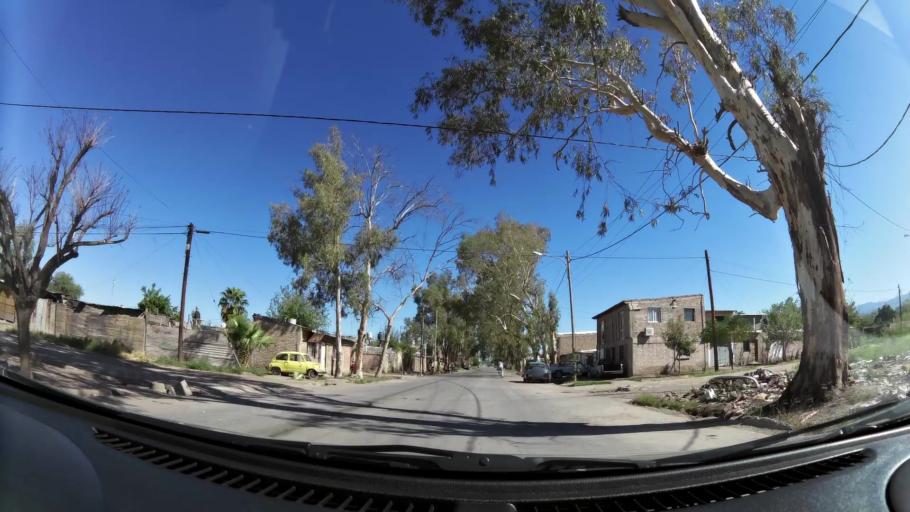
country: AR
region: Mendoza
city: Las Heras
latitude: -32.8301
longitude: -68.8165
